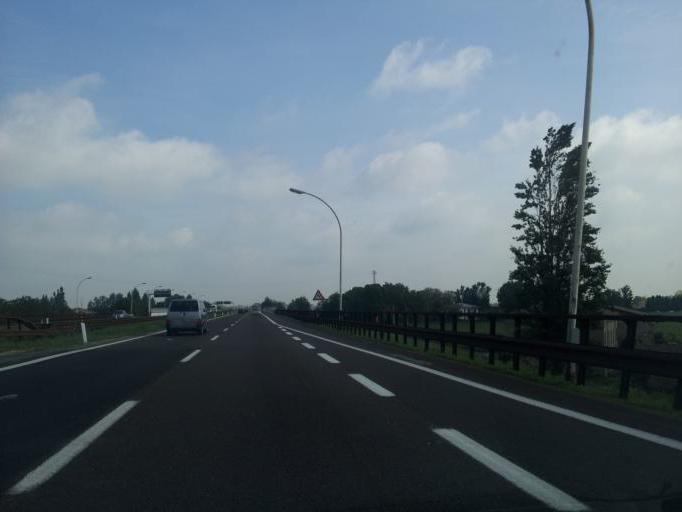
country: IT
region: Lombardy
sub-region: Provincia di Mantova
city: Bondeno
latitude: 44.9131
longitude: 10.8498
